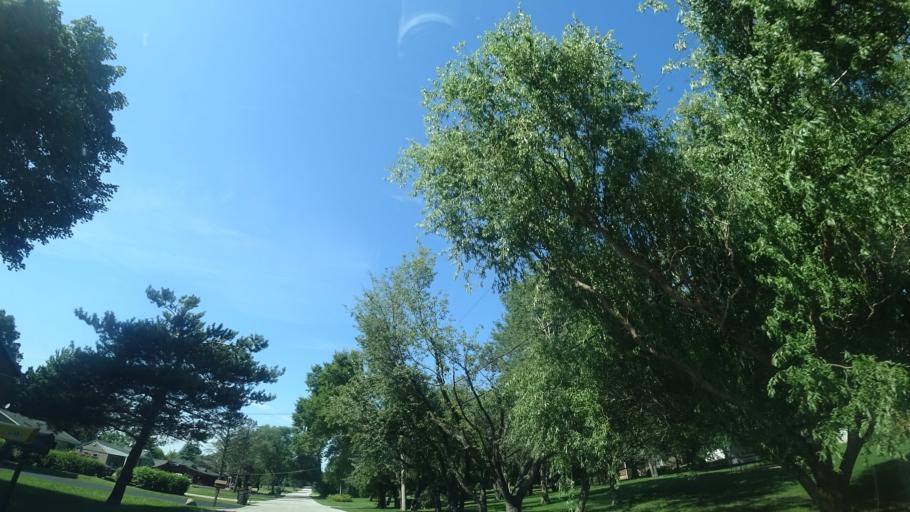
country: US
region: Illinois
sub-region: Will County
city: Mokena
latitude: 41.5718
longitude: -87.8870
